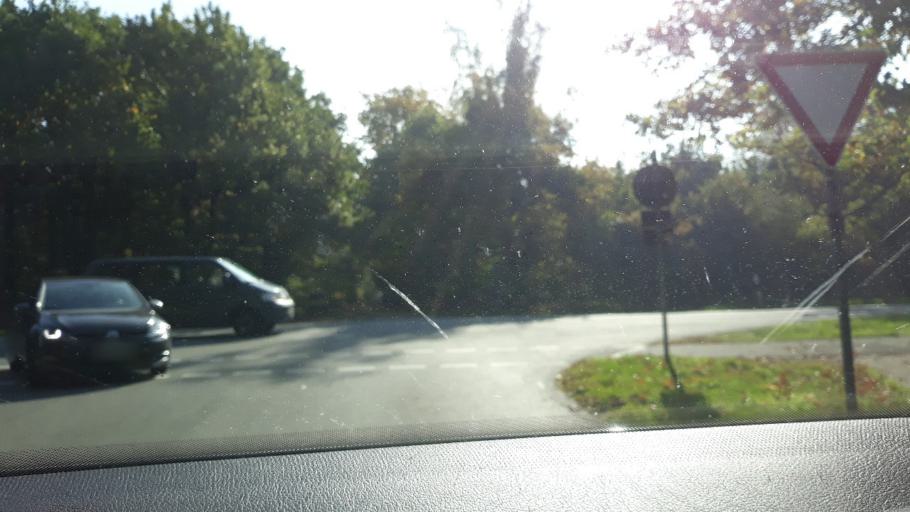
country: DE
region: Schleswig-Holstein
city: Kropp
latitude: 54.4034
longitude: 9.5042
